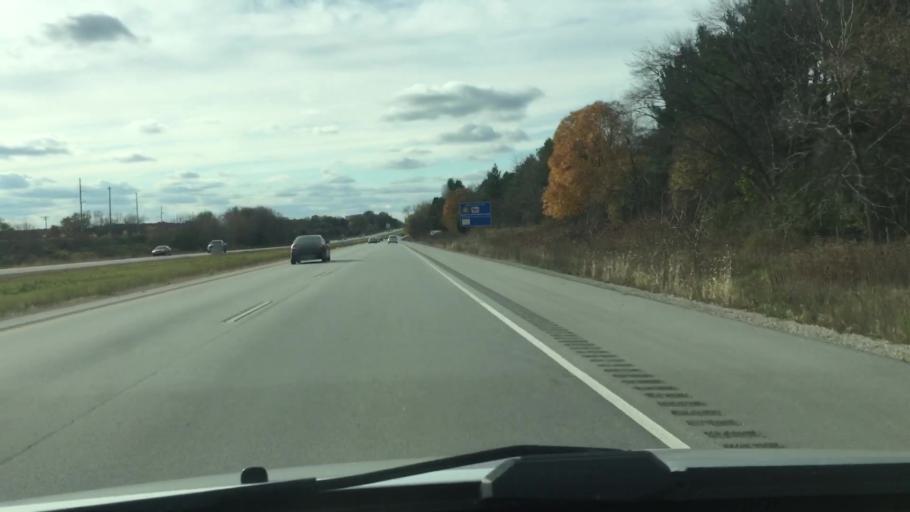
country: US
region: Wisconsin
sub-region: Waukesha County
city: Nashotah
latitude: 43.1029
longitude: -88.3796
